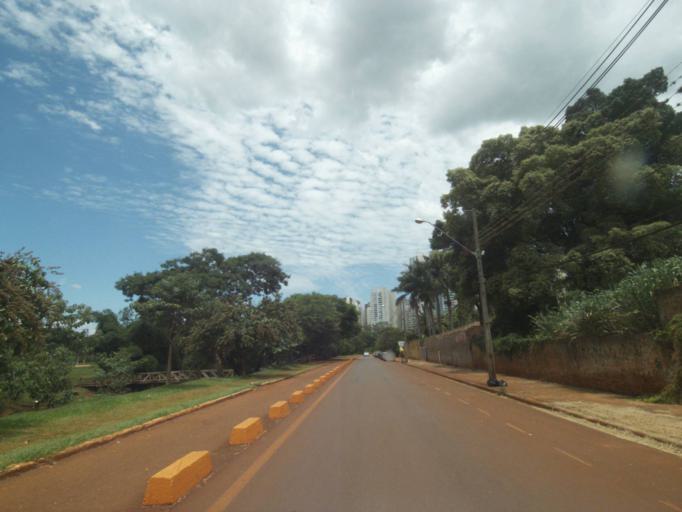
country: BR
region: Parana
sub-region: Londrina
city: Londrina
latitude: -23.3220
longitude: -51.1825
